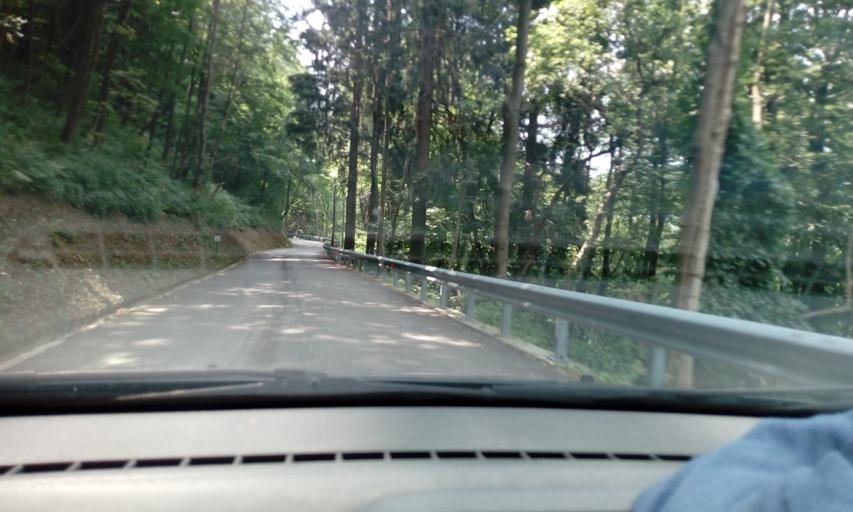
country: IT
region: Friuli Venezia Giulia
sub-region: Provincia di Udine
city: Cras
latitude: 46.1793
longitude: 13.6507
